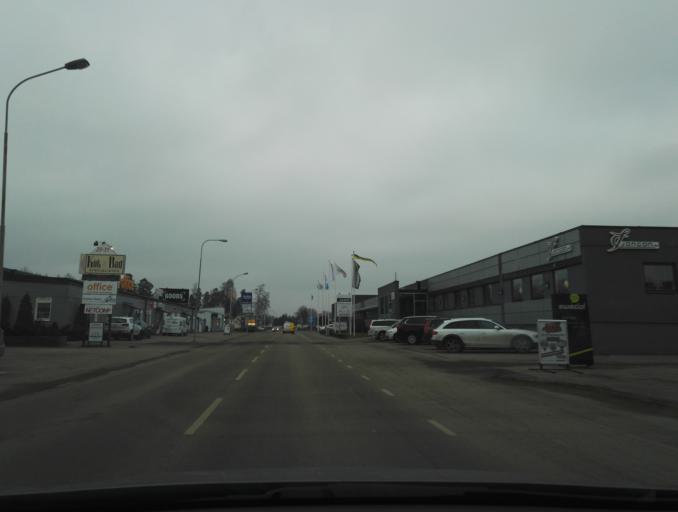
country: SE
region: Kronoberg
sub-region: Vaxjo Kommun
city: Vaexjoe
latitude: 56.8846
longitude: 14.7799
